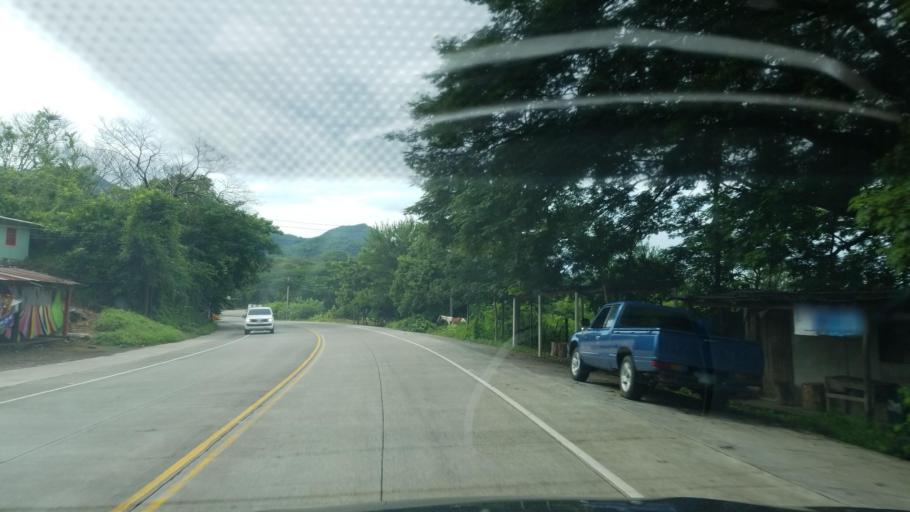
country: HN
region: Choluteca
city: Pespire
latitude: 13.6207
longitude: -87.3729
